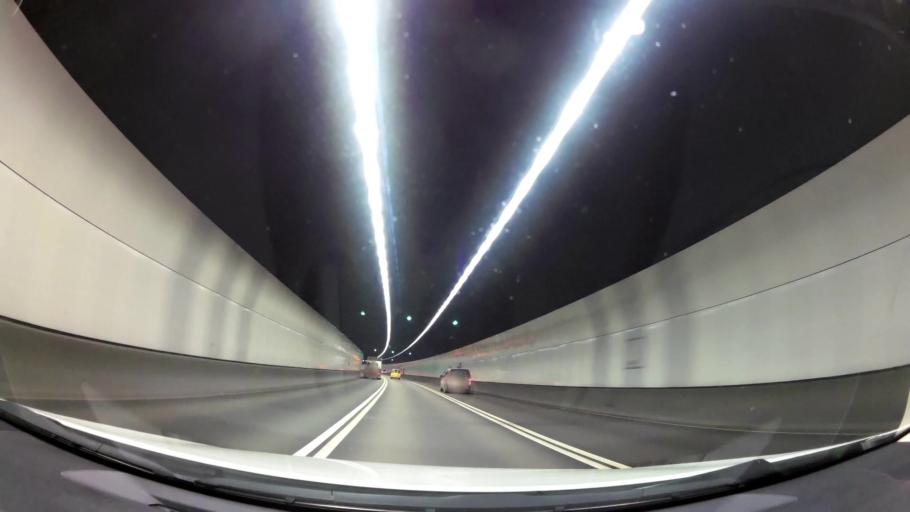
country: HK
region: Tsuen Wan
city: Tsuen Wan
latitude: 22.3467
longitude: 114.1038
